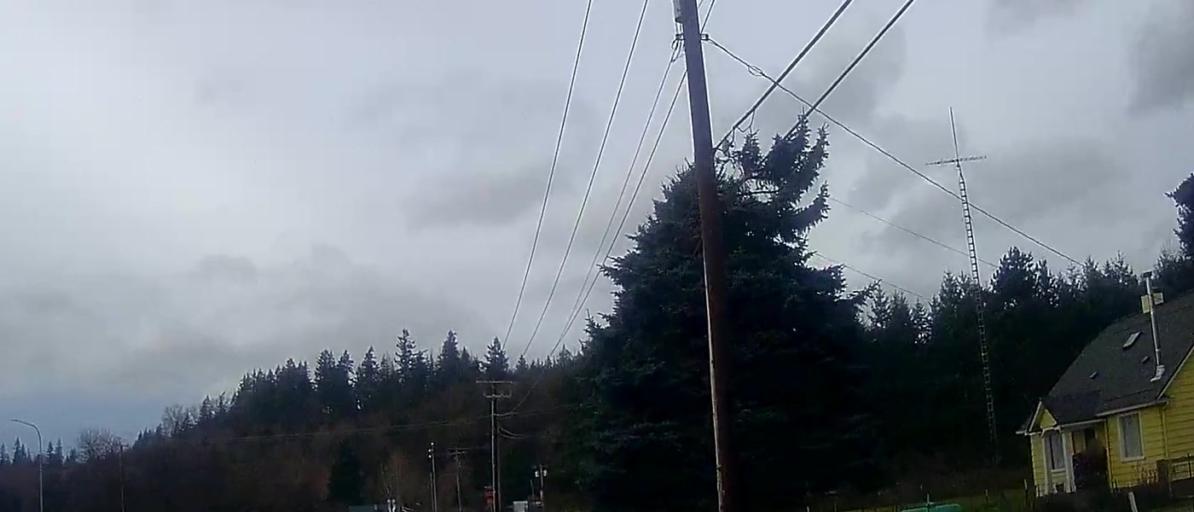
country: US
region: Washington
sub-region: Skagit County
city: Burlington
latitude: 48.5586
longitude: -122.3309
